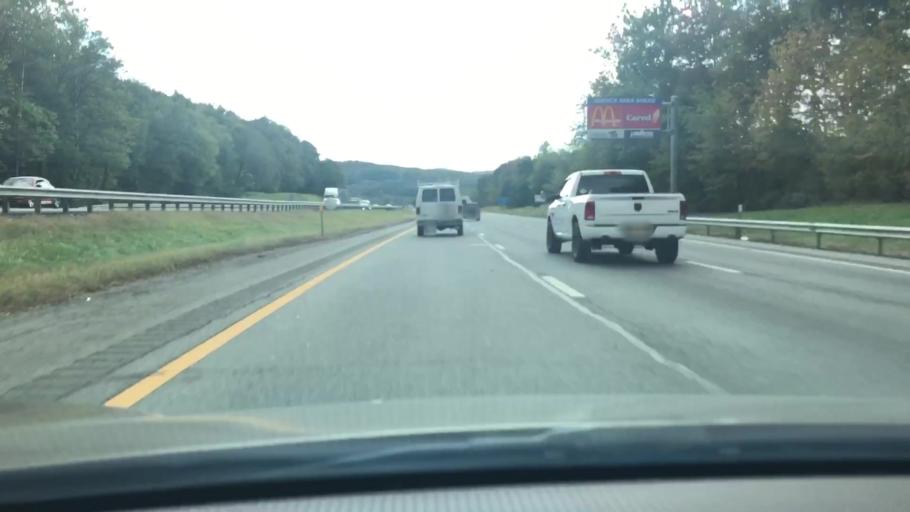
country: US
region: New York
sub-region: Rockland County
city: Sloatsburg
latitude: 41.1597
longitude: -74.1858
